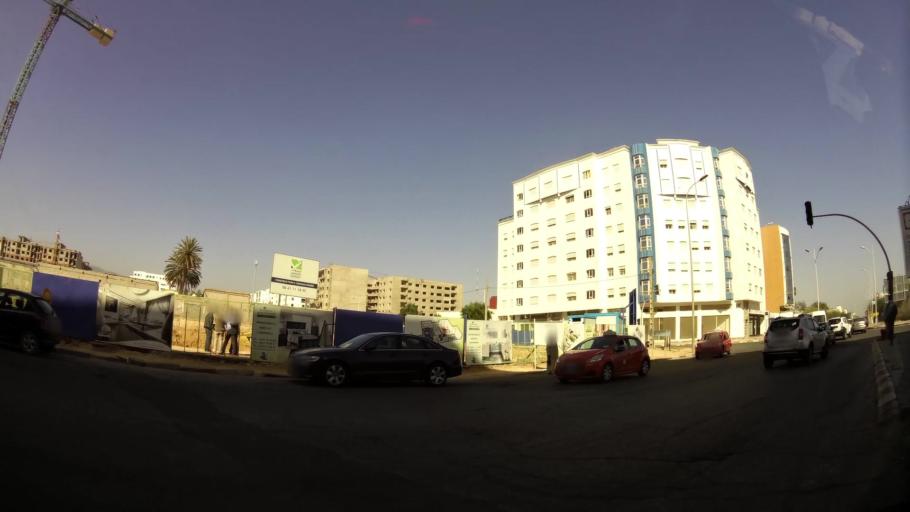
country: MA
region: Souss-Massa-Draa
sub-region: Agadir-Ida-ou-Tnan
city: Agadir
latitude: 30.4180
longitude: -9.5765
